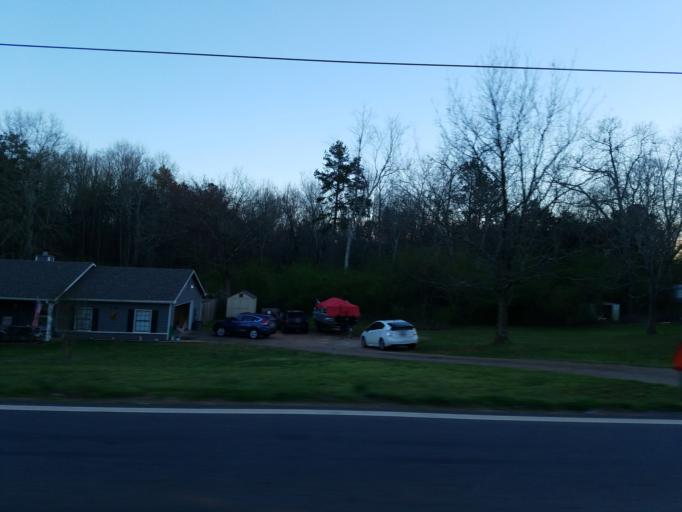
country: US
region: Georgia
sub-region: Hall County
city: Flowery Branch
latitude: 34.2909
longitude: -84.0198
